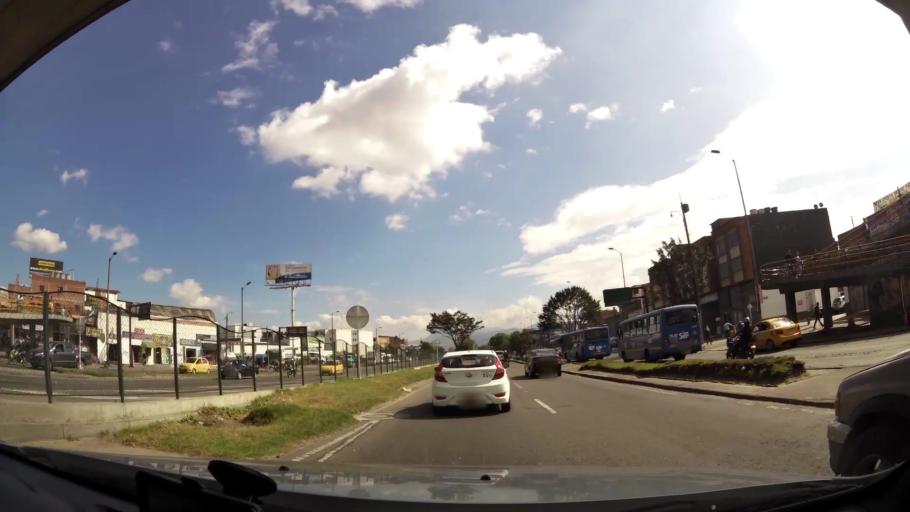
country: CO
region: Bogota D.C.
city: Bogota
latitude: 4.6184
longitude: -74.1396
